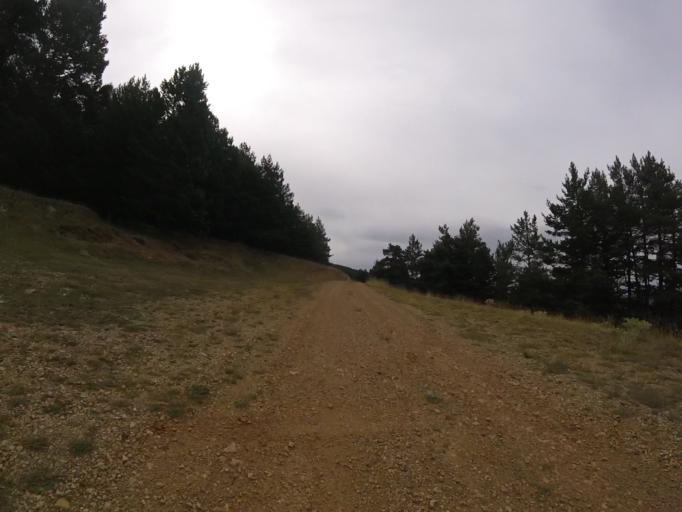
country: ES
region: Aragon
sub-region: Provincia de Teruel
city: Valdelinares
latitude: 40.3578
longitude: -0.6004
